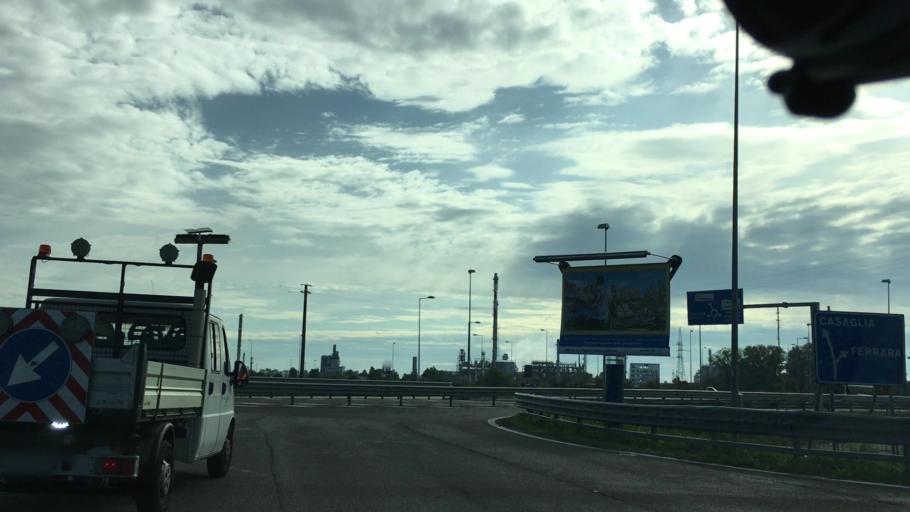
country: IT
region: Emilia-Romagna
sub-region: Provincia di Ferrara
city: Porotto-Cassama
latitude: 44.8664
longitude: 11.5735
